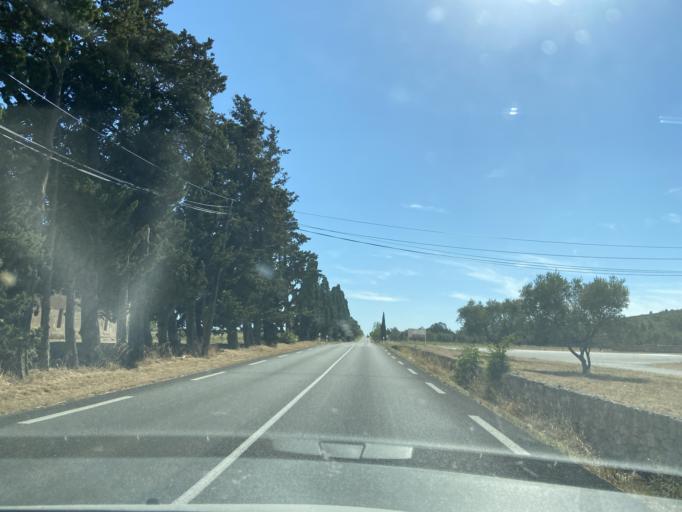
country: FR
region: Provence-Alpes-Cote d'Azur
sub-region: Departement des Bouches-du-Rhone
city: Lancon-Provence
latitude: 43.5454
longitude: 5.1377
